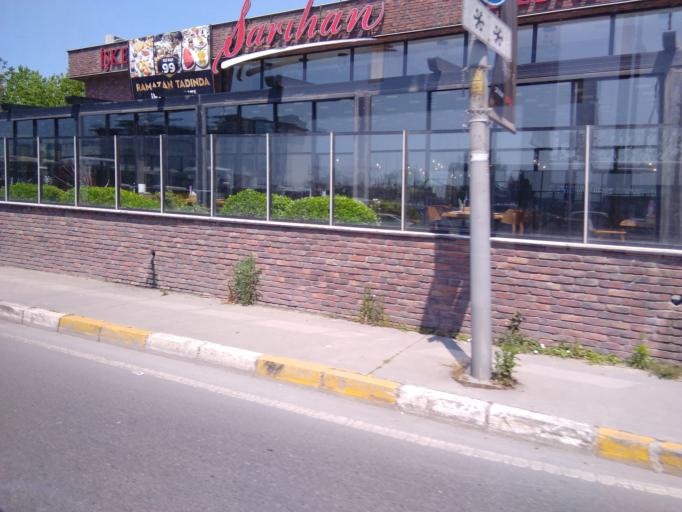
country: TR
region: Istanbul
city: Bahcelievler
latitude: 40.9934
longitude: 28.8263
